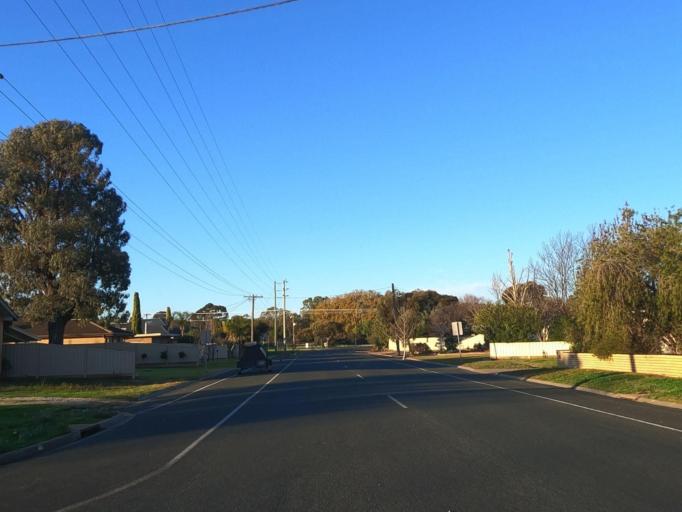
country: AU
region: Victoria
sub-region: Swan Hill
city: Swan Hill
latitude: -35.3591
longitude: 143.5606
